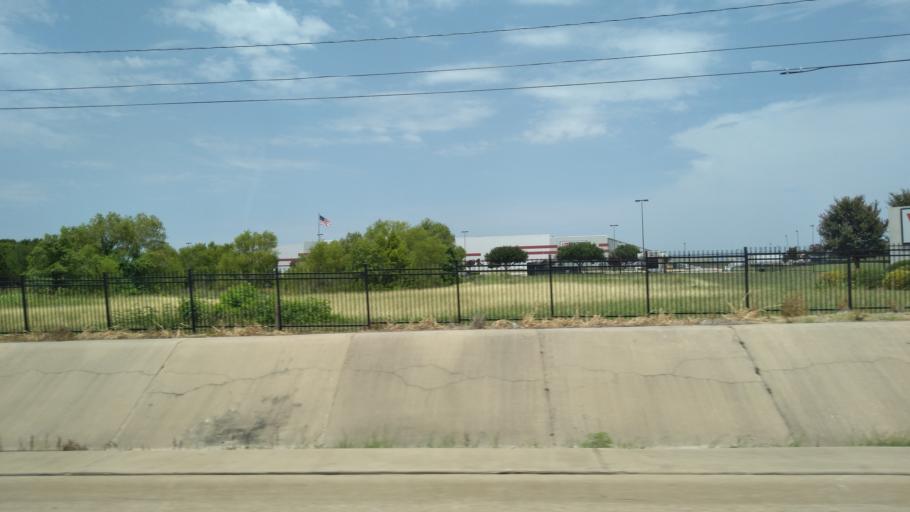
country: US
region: Texas
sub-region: McLennan County
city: Beverly Hills
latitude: 31.4851
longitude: -97.1563
